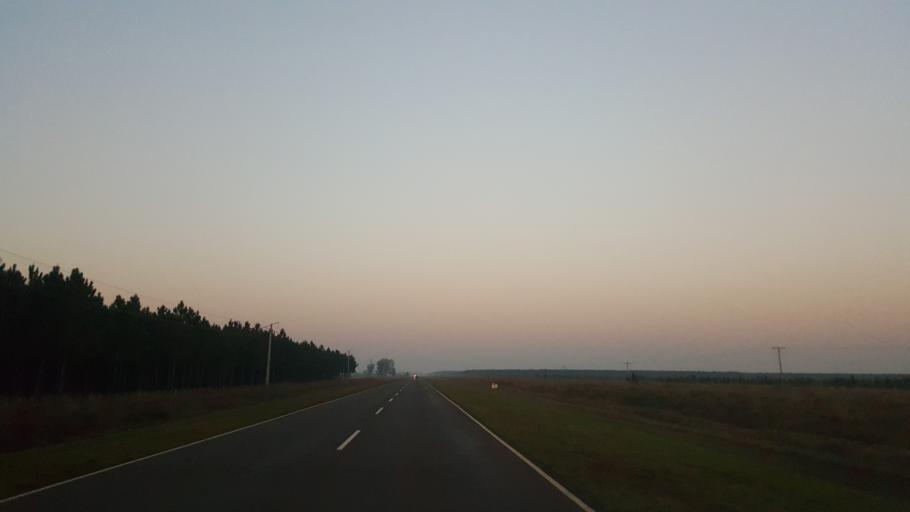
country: PY
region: Itapua
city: San Cosme y Damian
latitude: -27.5622
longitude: -56.2518
